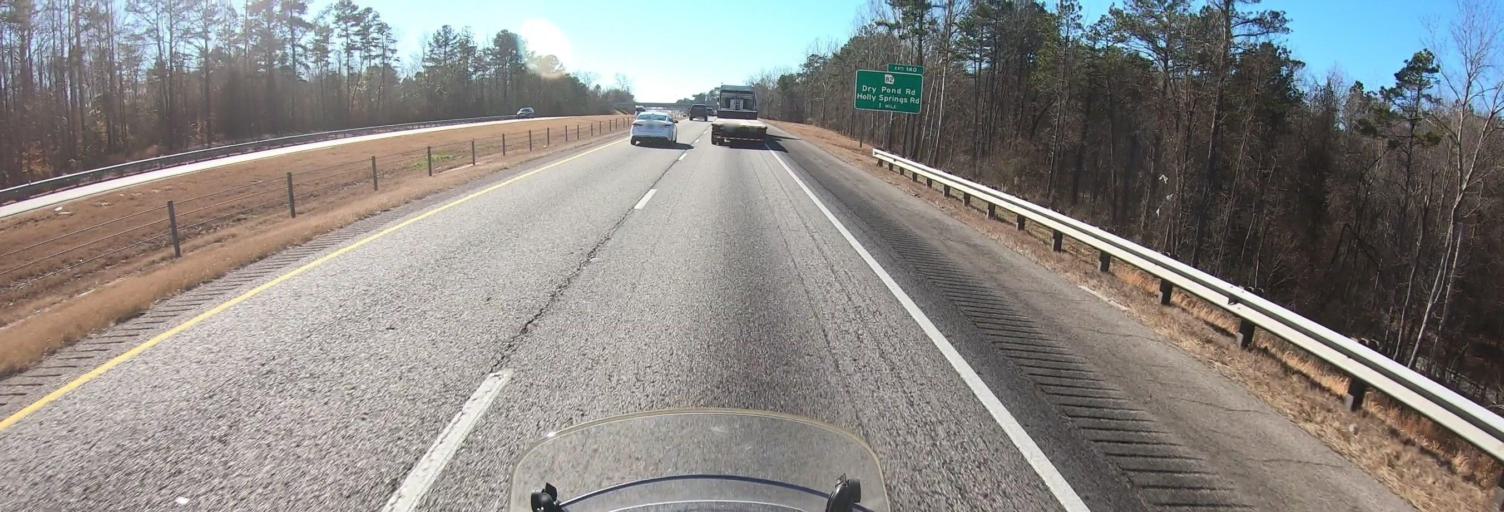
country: US
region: Georgia
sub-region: Banks County
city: Maysville
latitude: 34.1964
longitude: -83.5754
